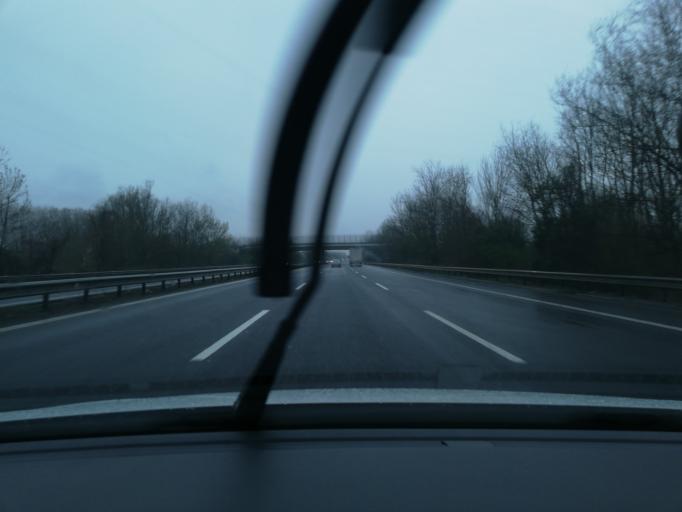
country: TR
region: Sakarya
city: Karapurcek
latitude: 40.7133
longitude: 30.4970
